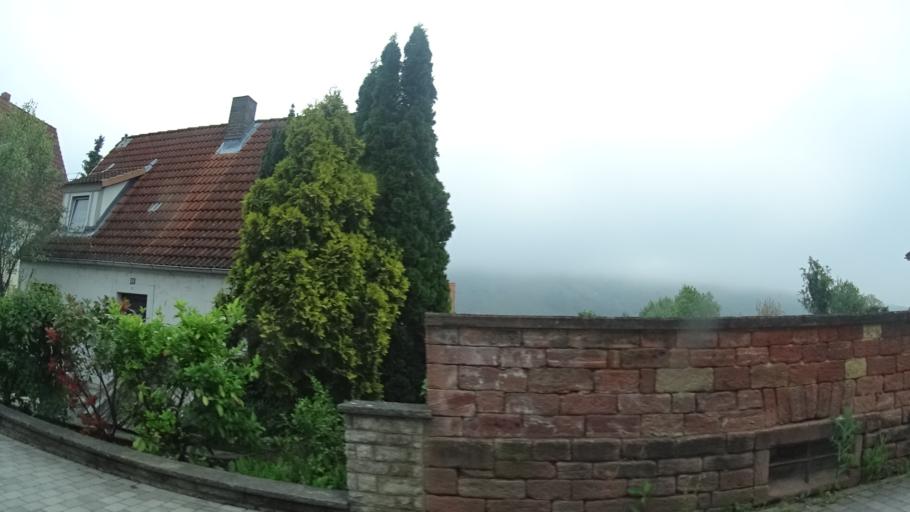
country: DE
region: Bavaria
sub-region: Regierungsbezirk Unterfranken
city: Klingenberg am Main
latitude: 49.7746
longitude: 9.1774
